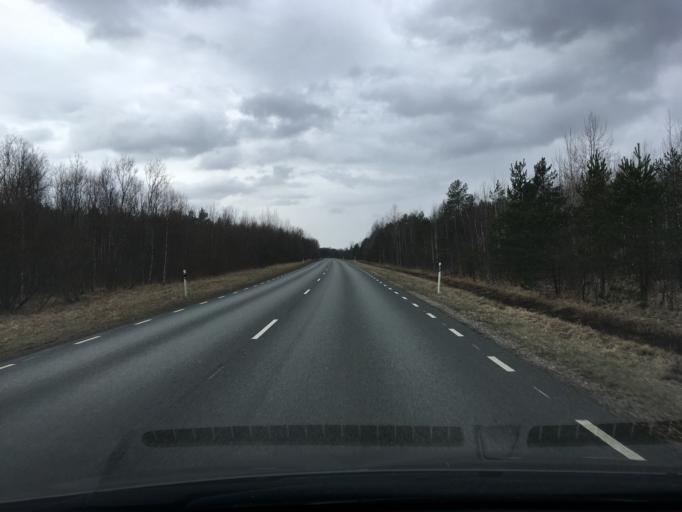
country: EE
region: Laeaene
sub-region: Lihula vald
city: Lihula
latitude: 58.6239
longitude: 23.8954
